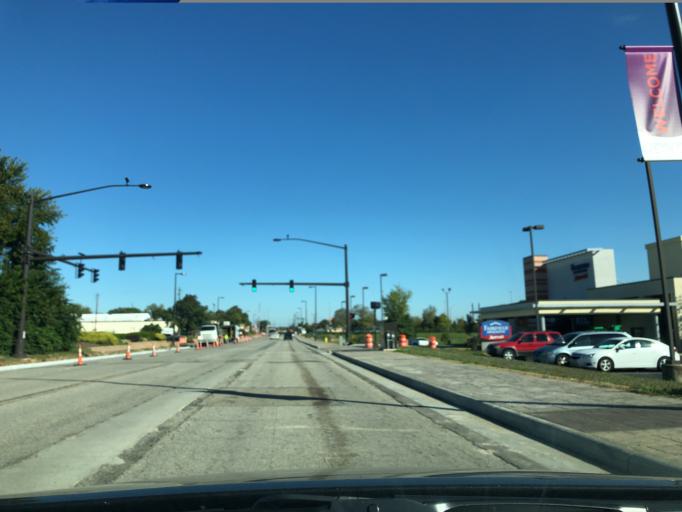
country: US
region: Ohio
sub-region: Hamilton County
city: Glendale
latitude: 39.2808
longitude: -84.4434
